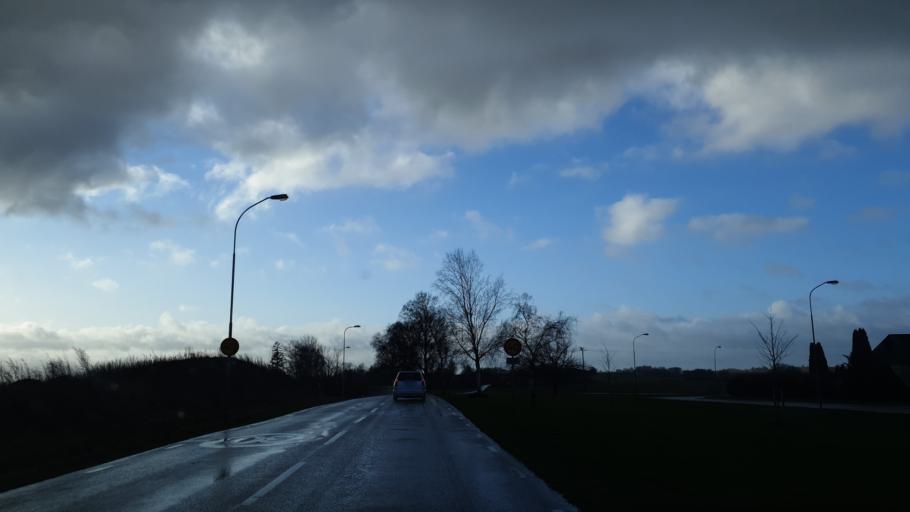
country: SE
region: Skane
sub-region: Skurups Kommun
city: Rydsgard
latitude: 55.4695
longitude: 13.5764
